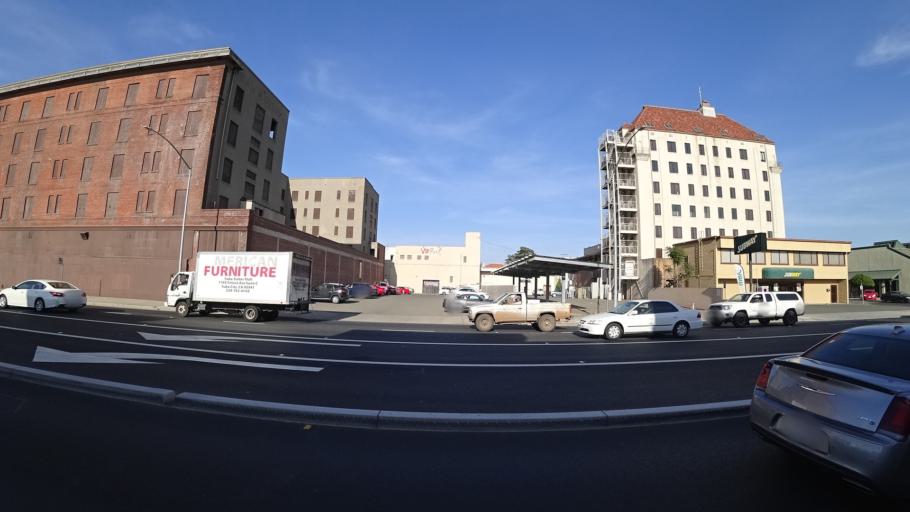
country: US
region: California
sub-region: Yuba County
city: Marysville
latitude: 39.1397
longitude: -121.5906
